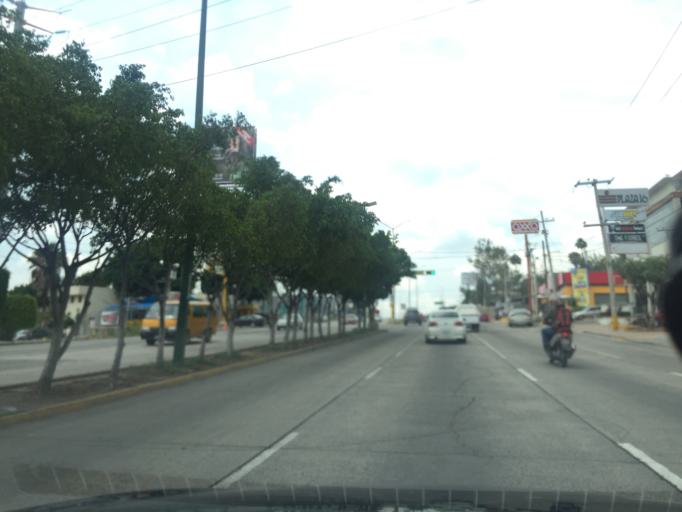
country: MX
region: Guanajuato
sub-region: Leon
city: La Ermita
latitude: 21.1467
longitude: -101.7102
